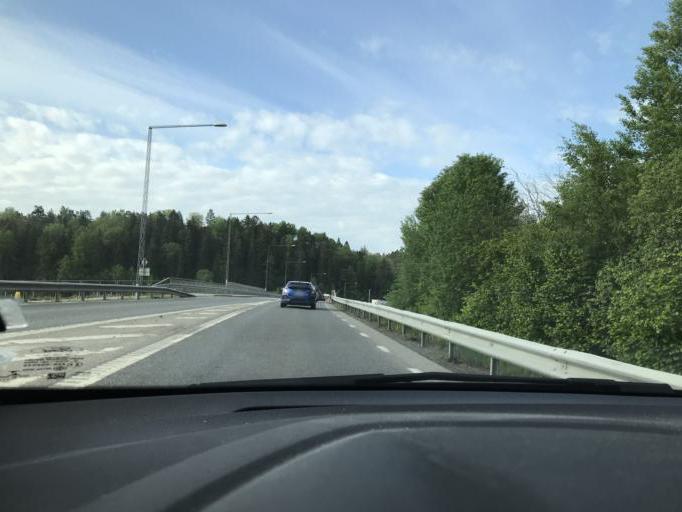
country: SE
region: Stockholm
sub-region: Botkyrka Kommun
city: Tumba
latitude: 59.2004
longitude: 17.8417
